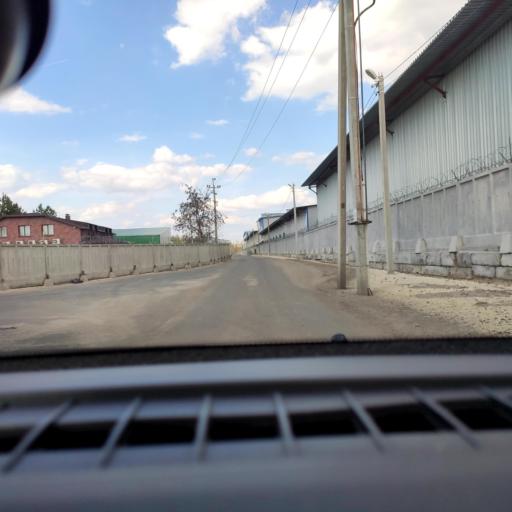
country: RU
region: Voronezj
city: Podgornoye
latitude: 51.7992
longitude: 39.1925
